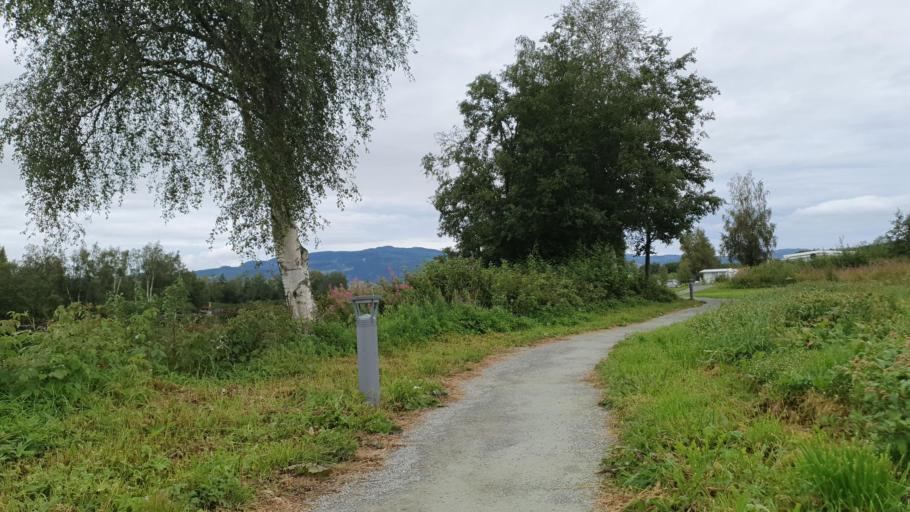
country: NO
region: Sor-Trondelag
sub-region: Selbu
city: Mebonden
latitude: 63.2274
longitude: 11.0234
